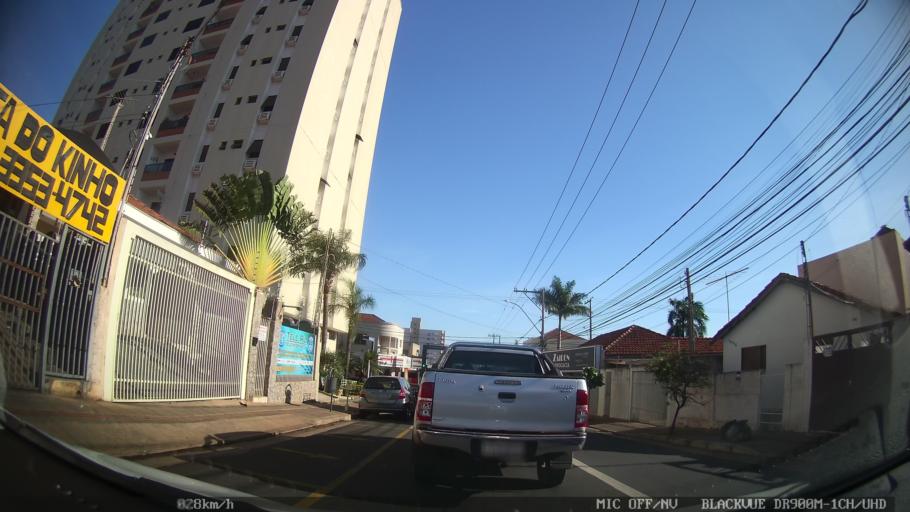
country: BR
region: Sao Paulo
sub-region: Sao Jose Do Rio Preto
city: Sao Jose do Rio Preto
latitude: -20.8021
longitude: -49.3723
